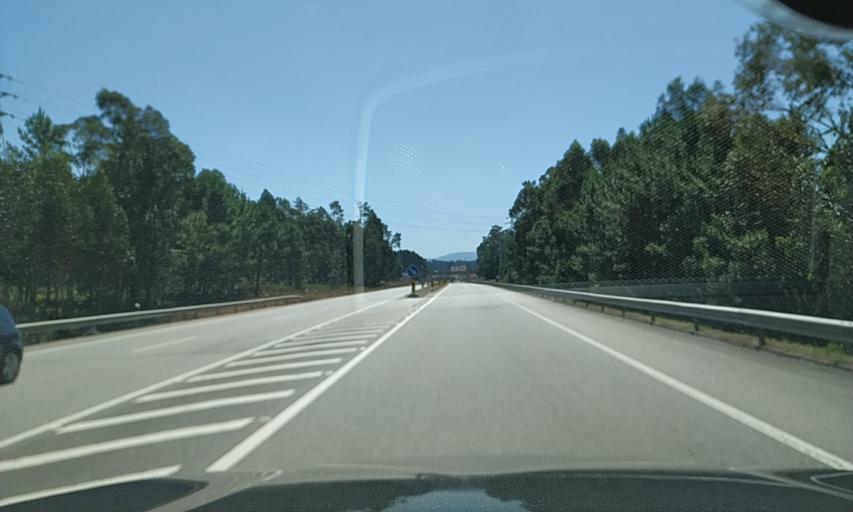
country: PT
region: Aveiro
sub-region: Agueda
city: Aguada de Cima
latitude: 40.5264
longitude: -8.4529
